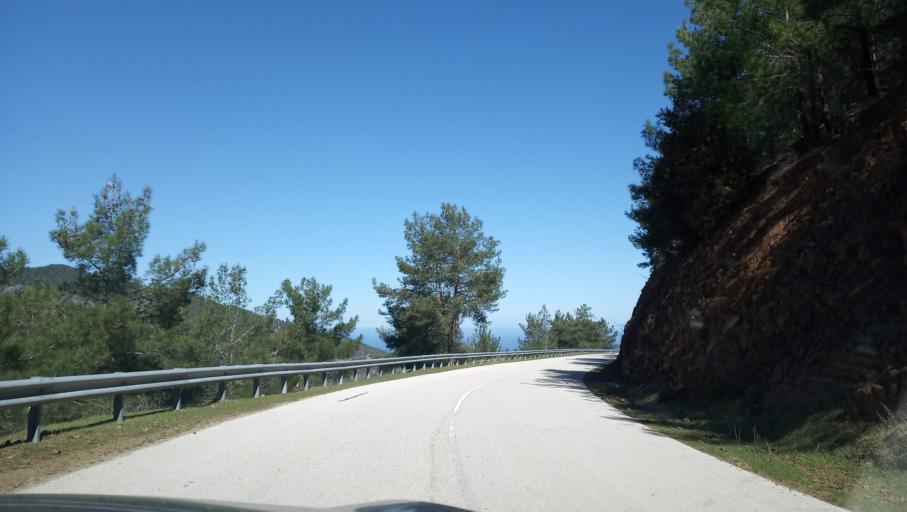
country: CY
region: Lefkosia
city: Lefka
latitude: 35.0692
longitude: 32.7594
